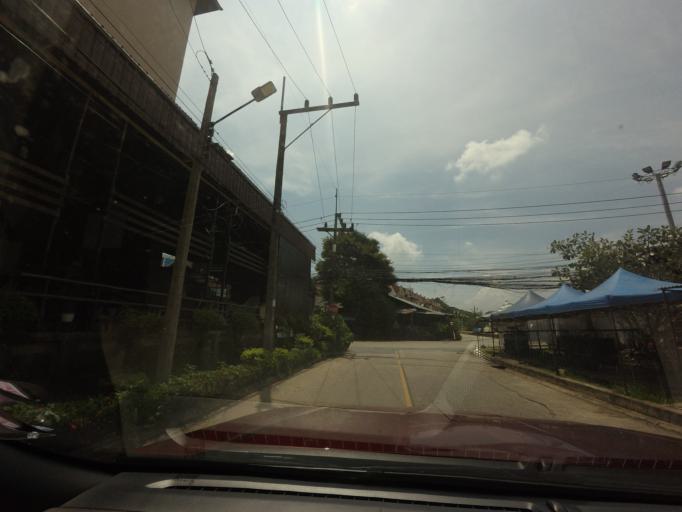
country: TH
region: Yala
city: Betong
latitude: 5.7692
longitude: 101.0743
